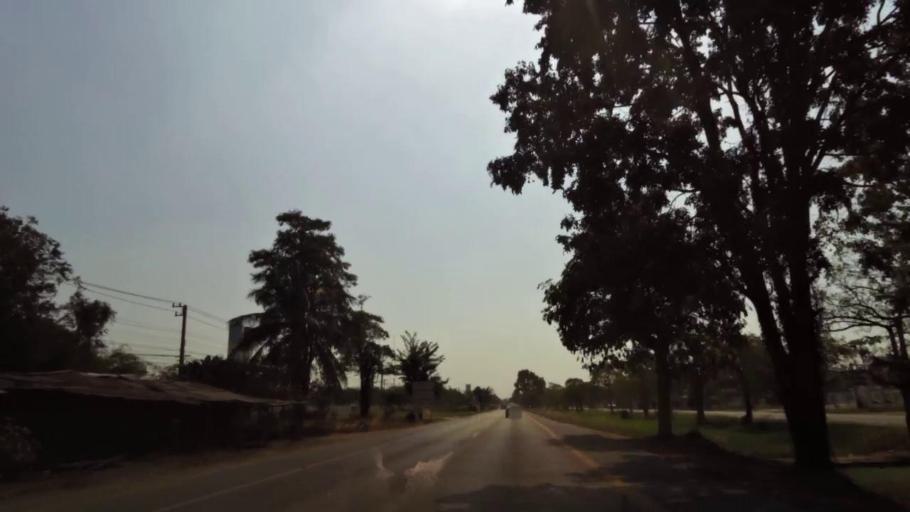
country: TH
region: Phichit
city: Wachira Barami
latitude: 16.5013
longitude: 100.1439
